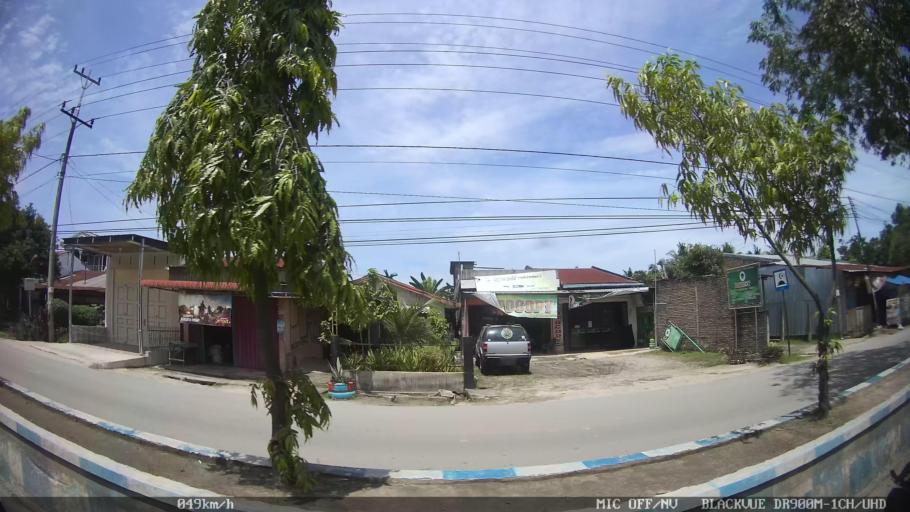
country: ID
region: North Sumatra
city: Percut
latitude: 3.5484
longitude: 98.8792
